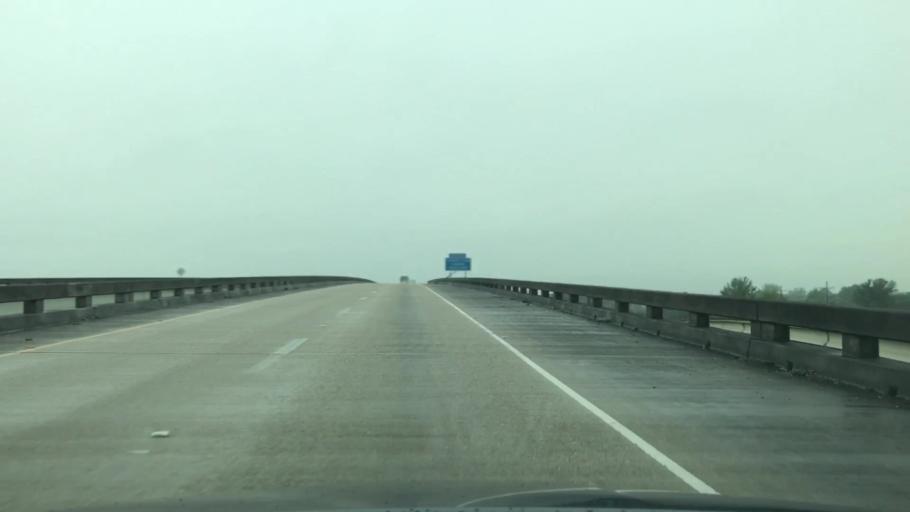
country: US
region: Louisiana
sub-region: Lafourche Parish
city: Mathews
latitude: 29.7105
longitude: -90.5698
